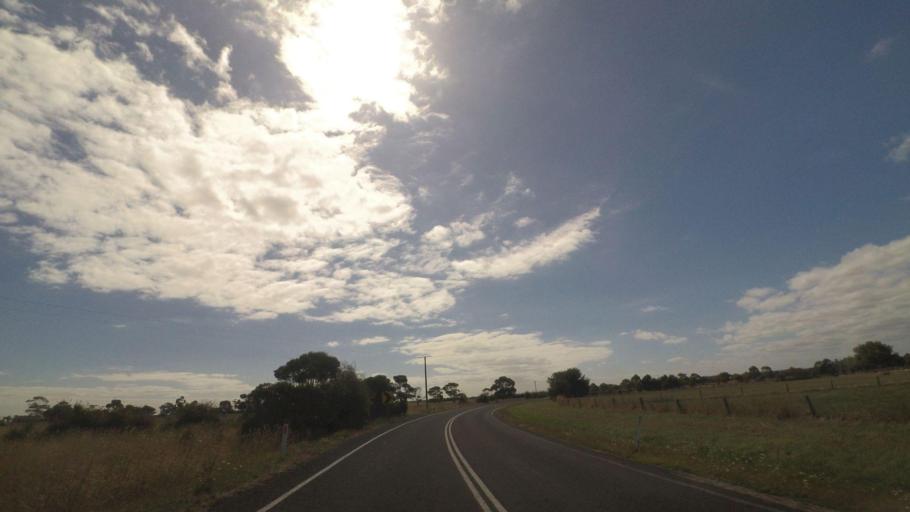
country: AU
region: Victoria
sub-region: Cardinia
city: Garfield
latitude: -38.2130
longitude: 145.6377
